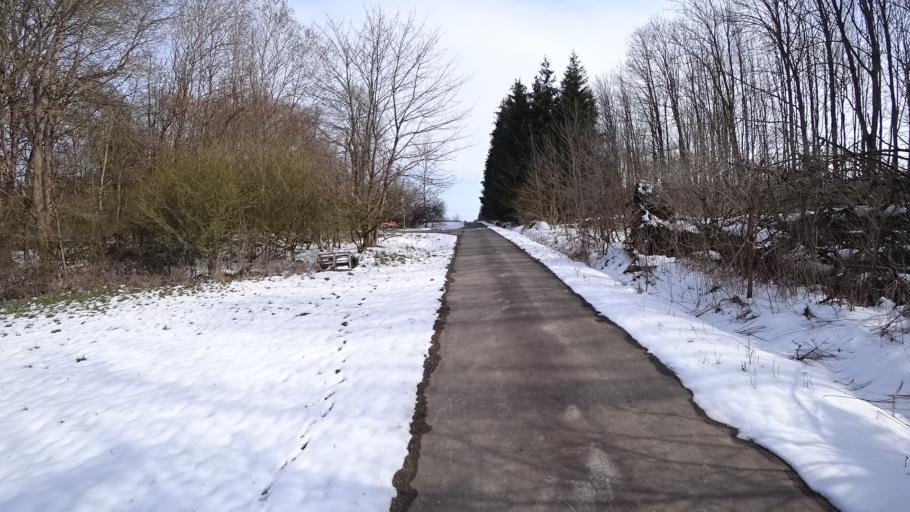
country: DE
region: Rheinland-Pfalz
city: Morlen
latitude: 50.6874
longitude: 7.8847
